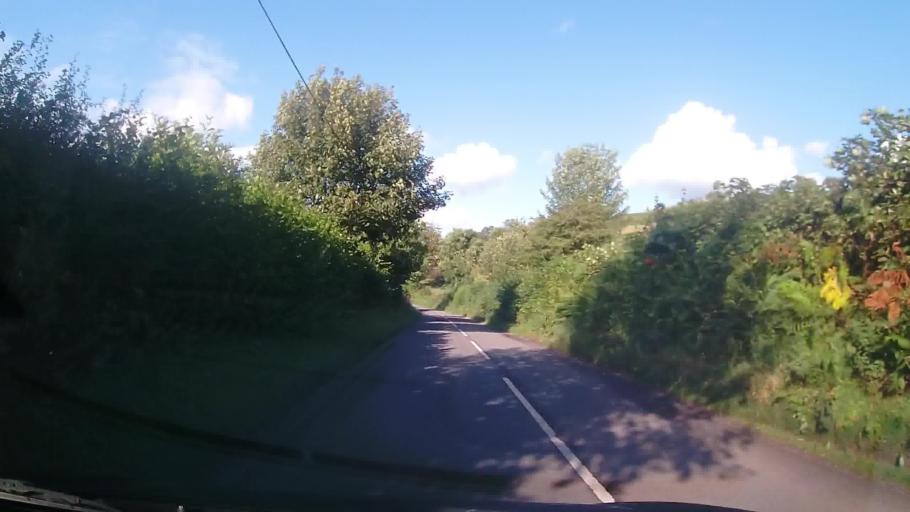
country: GB
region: England
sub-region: Shropshire
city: Norbury
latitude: 52.5708
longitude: -2.8913
